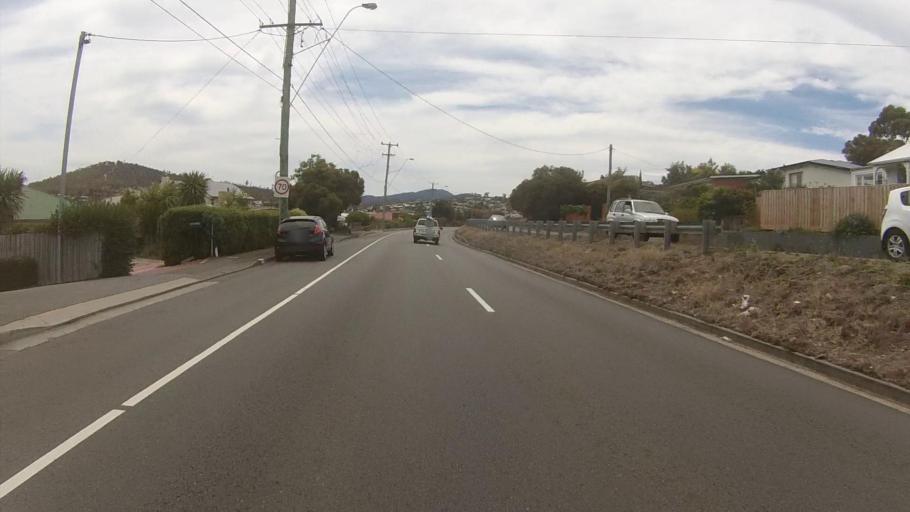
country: AU
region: Tasmania
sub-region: Clarence
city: Lindisfarne
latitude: -42.8560
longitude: 147.3567
